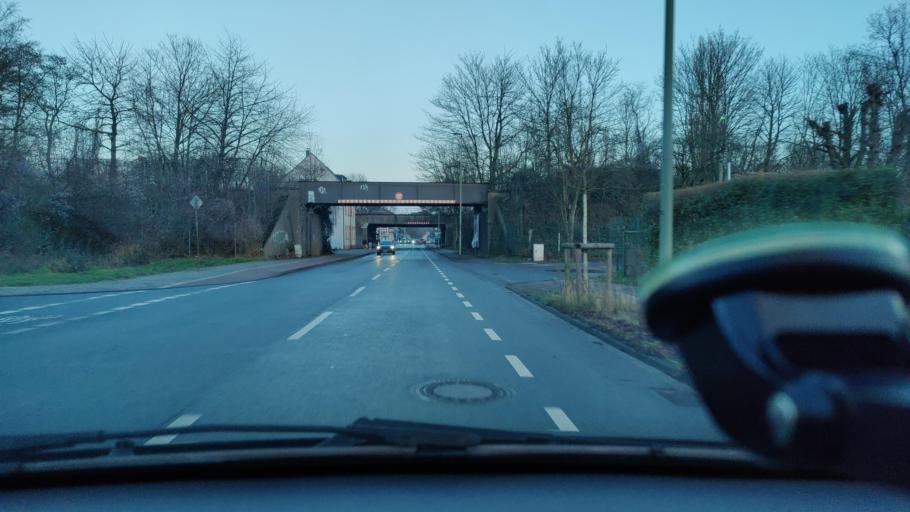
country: DE
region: North Rhine-Westphalia
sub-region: Regierungsbezirk Dusseldorf
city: Dinslaken
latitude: 51.5337
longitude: 6.7174
